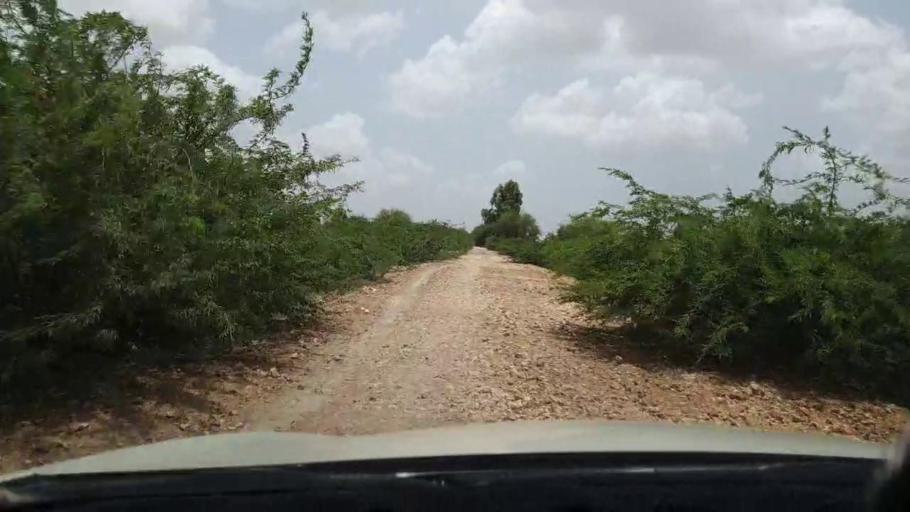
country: PK
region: Sindh
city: Kadhan
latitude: 24.3762
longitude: 68.9289
